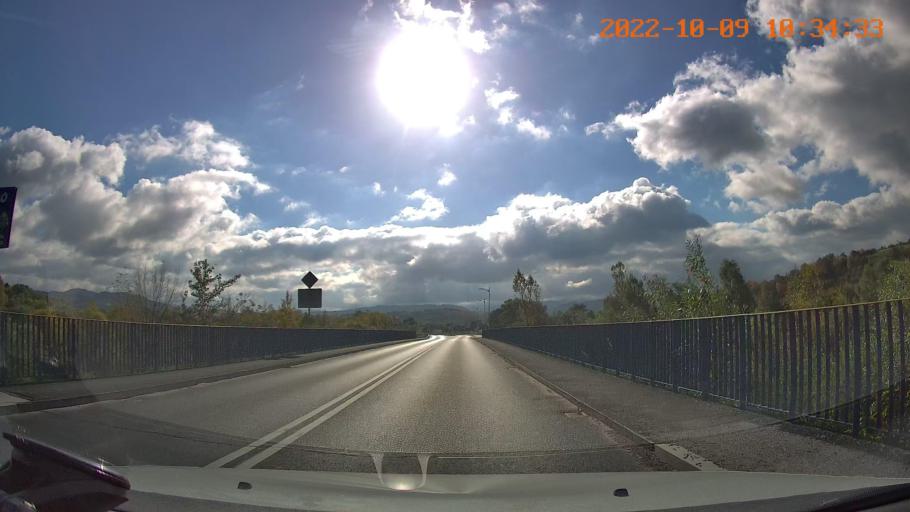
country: PL
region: Lesser Poland Voivodeship
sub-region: Powiat limanowski
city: Mszana Dolna
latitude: 49.6862
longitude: 20.0503
